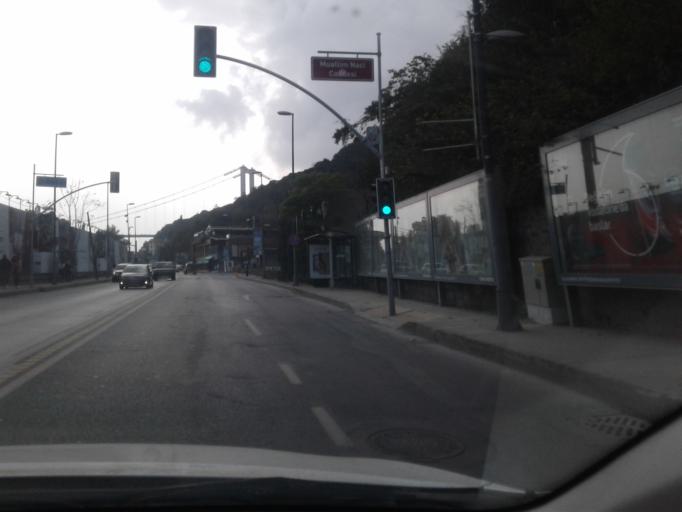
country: TR
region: Istanbul
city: UEskuedar
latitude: 41.0574
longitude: 29.0350
